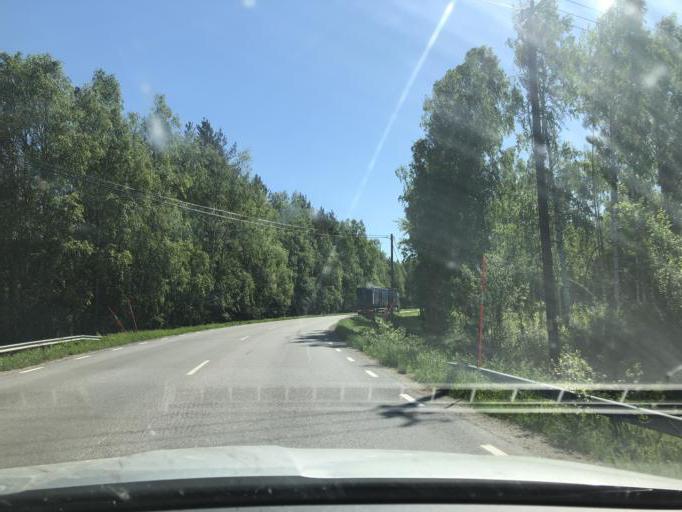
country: SE
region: Norrbotten
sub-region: Lulea Kommun
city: Sodra Sunderbyn
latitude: 65.6643
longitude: 21.9670
